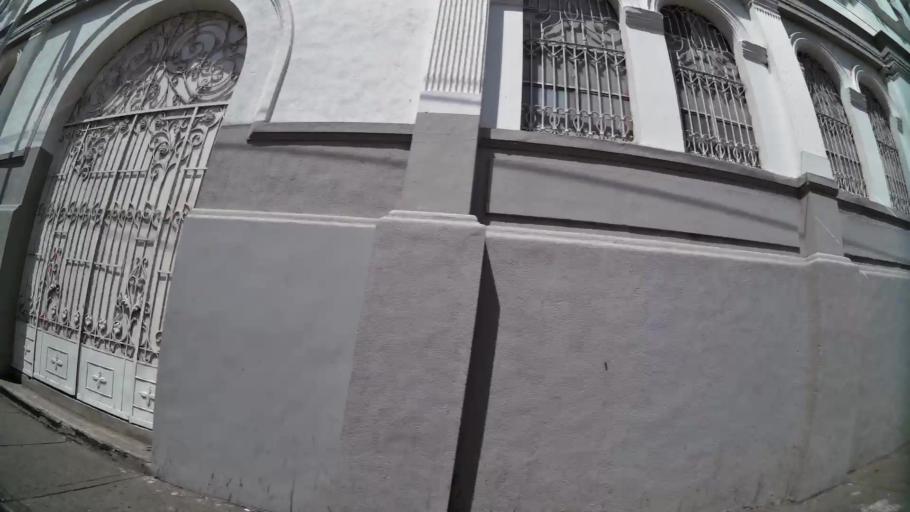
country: CO
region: Valle del Cauca
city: Cali
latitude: 3.4484
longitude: -76.5338
